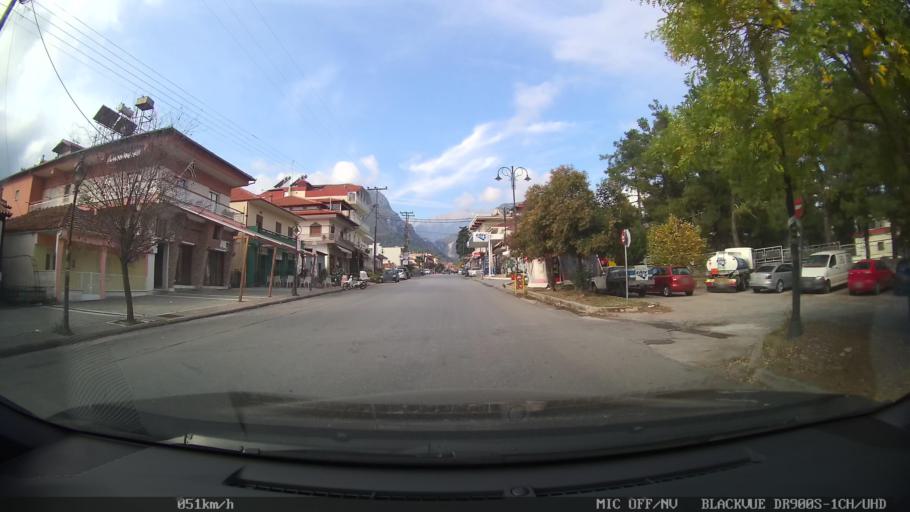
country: GR
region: Central Macedonia
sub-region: Nomos Pierias
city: Litochoro
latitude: 40.1062
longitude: 22.5089
